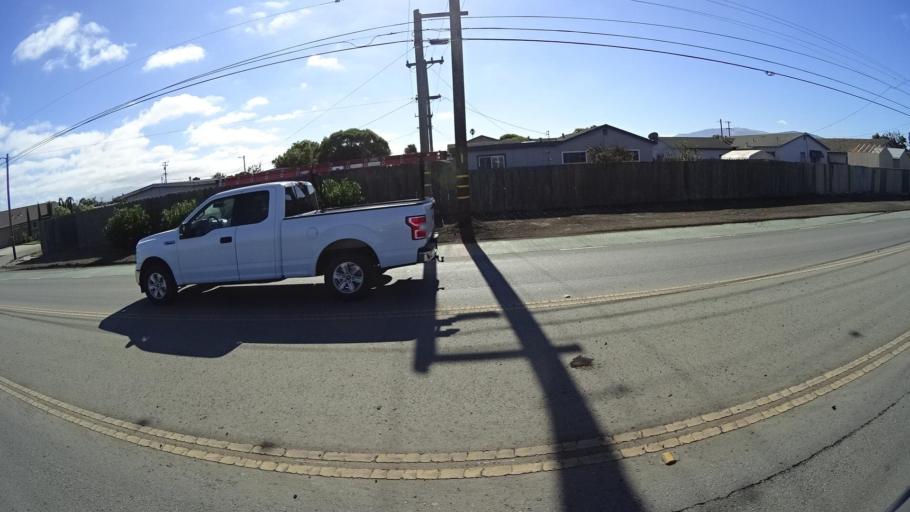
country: US
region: California
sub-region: Monterey County
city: Salinas
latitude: 36.6742
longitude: -121.6799
